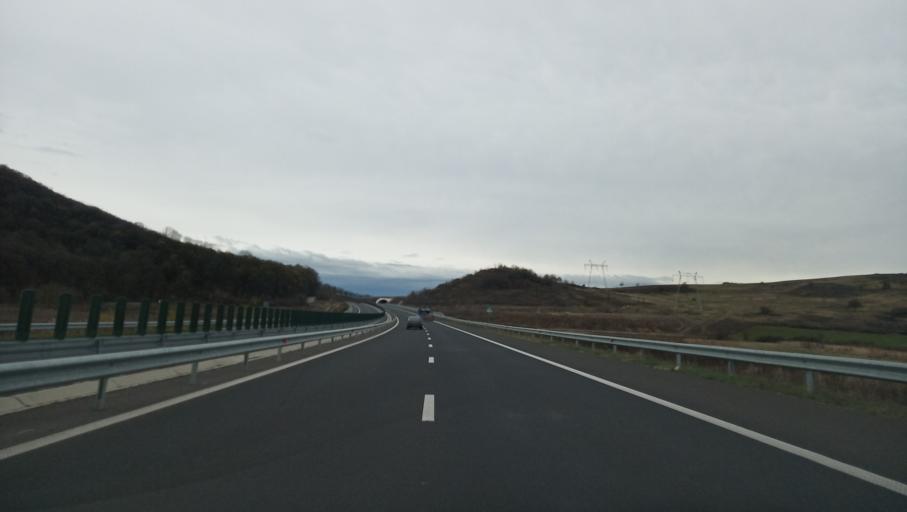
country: RO
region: Hunedoara
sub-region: Comuna Branisca
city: Branisca
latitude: 45.9369
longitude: 22.7497
